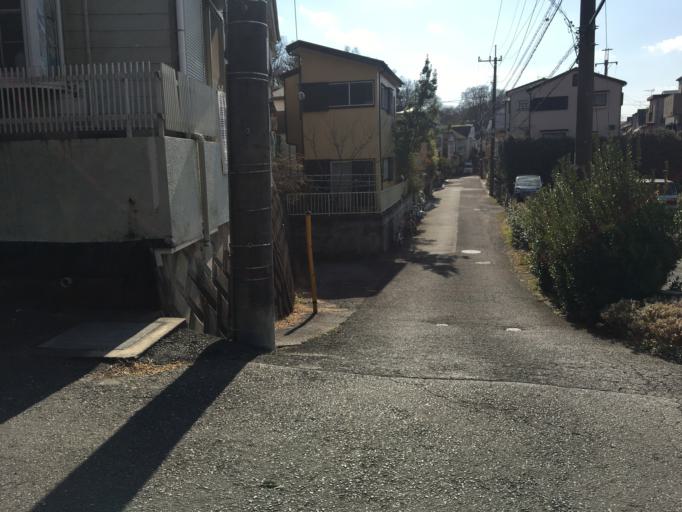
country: JP
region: Saitama
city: Oi
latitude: 35.8468
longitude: 139.5515
